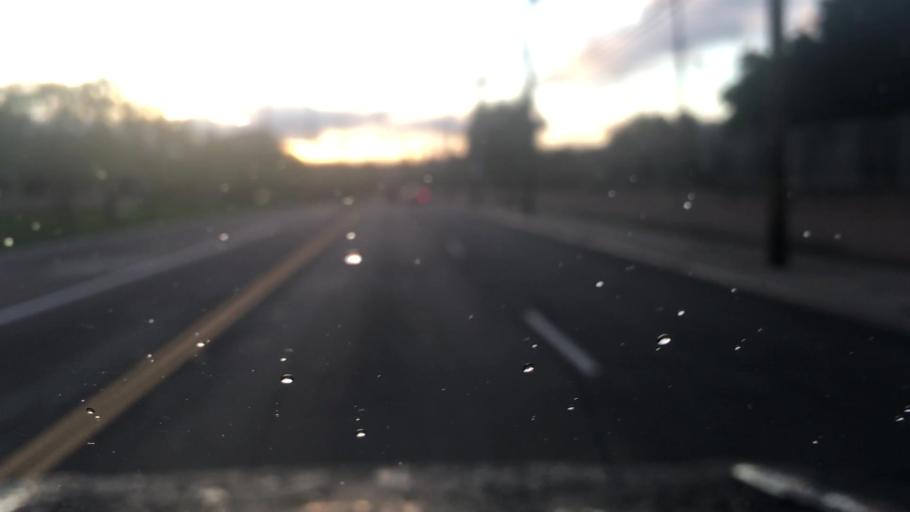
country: US
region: California
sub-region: Ventura County
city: Casa Conejo
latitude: 34.1902
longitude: -118.9438
